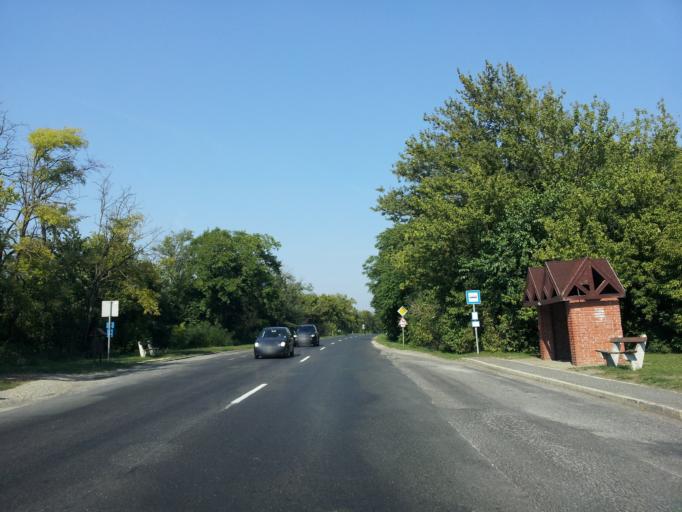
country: HU
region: Fejer
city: Enying
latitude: 46.9572
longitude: 18.1874
